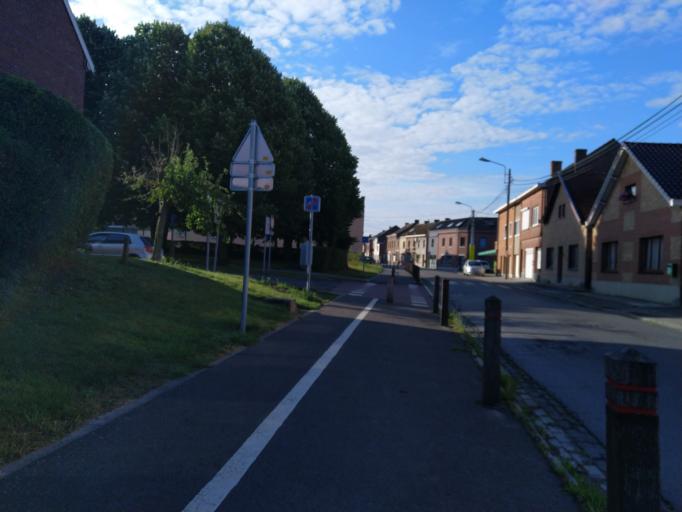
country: BE
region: Wallonia
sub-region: Province du Hainaut
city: Binche
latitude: 50.4379
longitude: 4.1481
